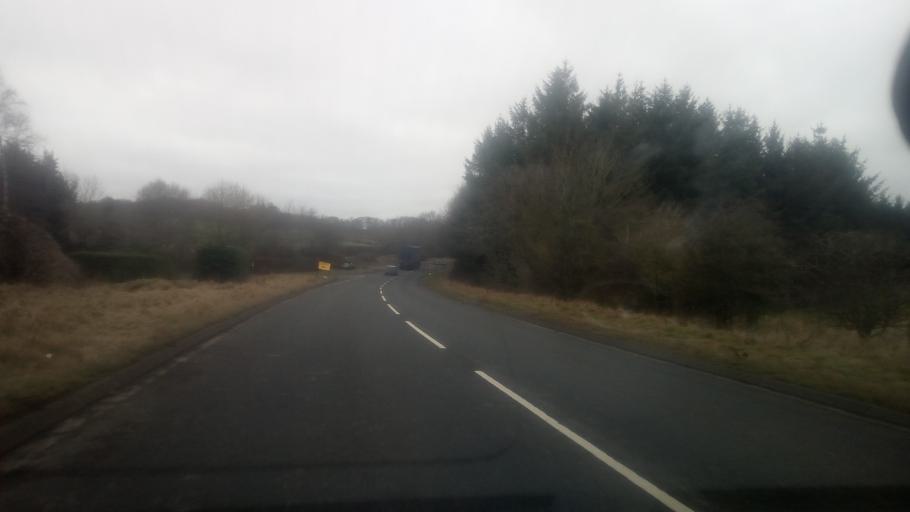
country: GB
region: Scotland
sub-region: The Scottish Borders
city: Kelso
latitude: 55.5750
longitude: -2.5170
